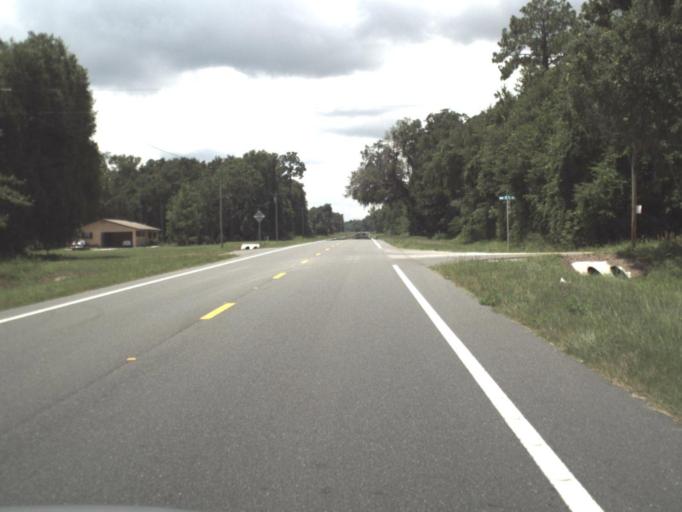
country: US
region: Florida
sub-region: Alachua County
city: Alachua
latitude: 29.8670
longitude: -82.3423
